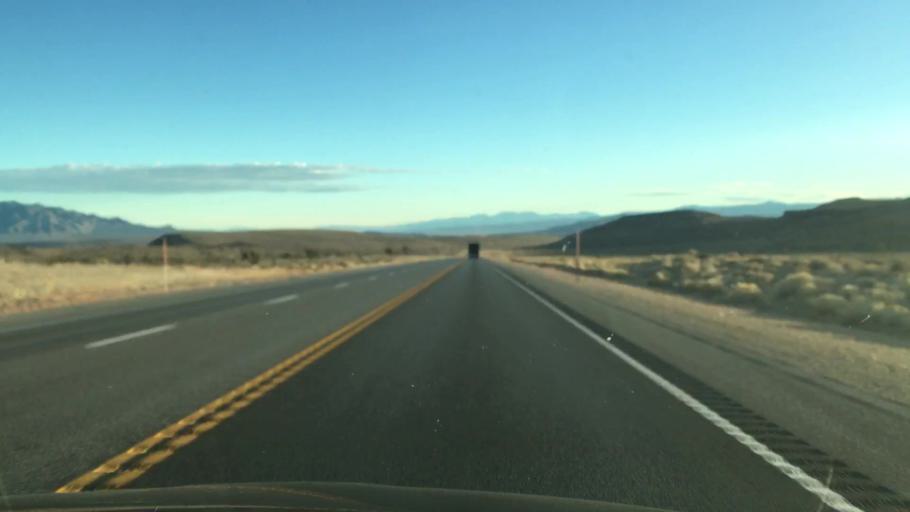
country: US
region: Nevada
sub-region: Esmeralda County
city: Goldfield
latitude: 37.6652
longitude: -117.2183
